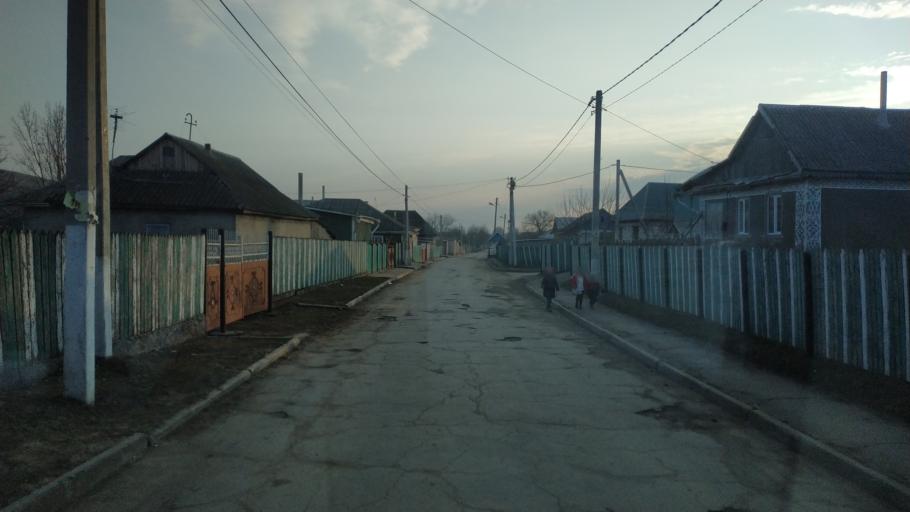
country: MD
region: Hincesti
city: Dancu
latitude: 46.7171
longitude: 28.3515
